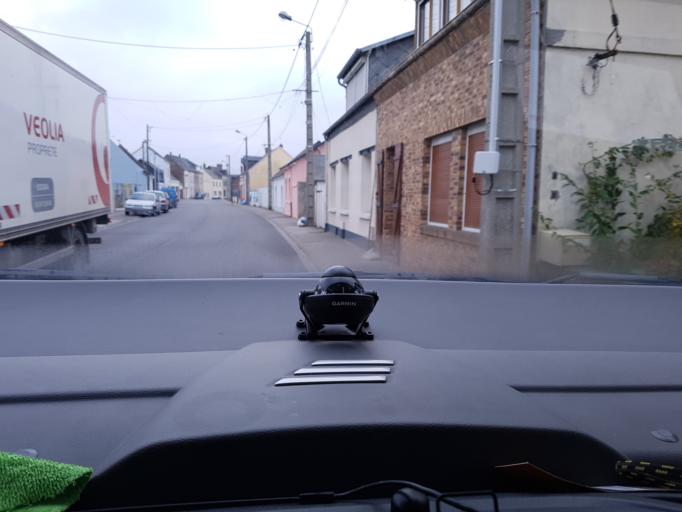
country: FR
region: Picardie
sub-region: Departement de la Somme
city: Cayeux-sur-Mer
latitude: 50.1756
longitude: 1.4945
